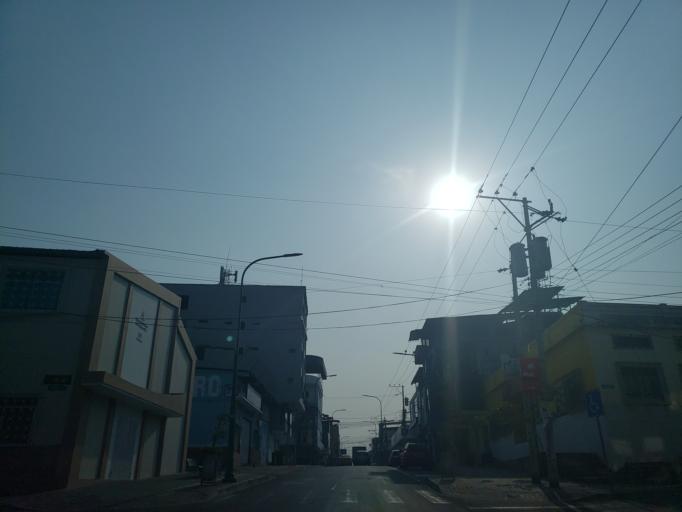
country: EC
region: Manabi
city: Manta
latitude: -0.9468
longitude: -80.7247
